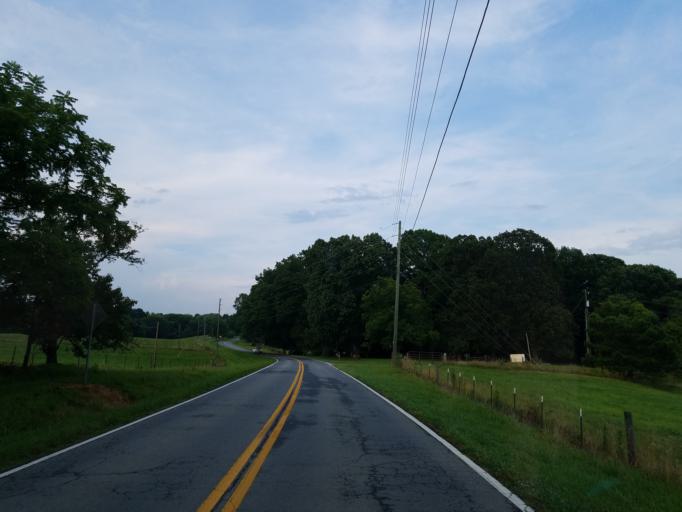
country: US
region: Georgia
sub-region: Pickens County
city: Jasper
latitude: 34.4576
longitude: -84.5340
